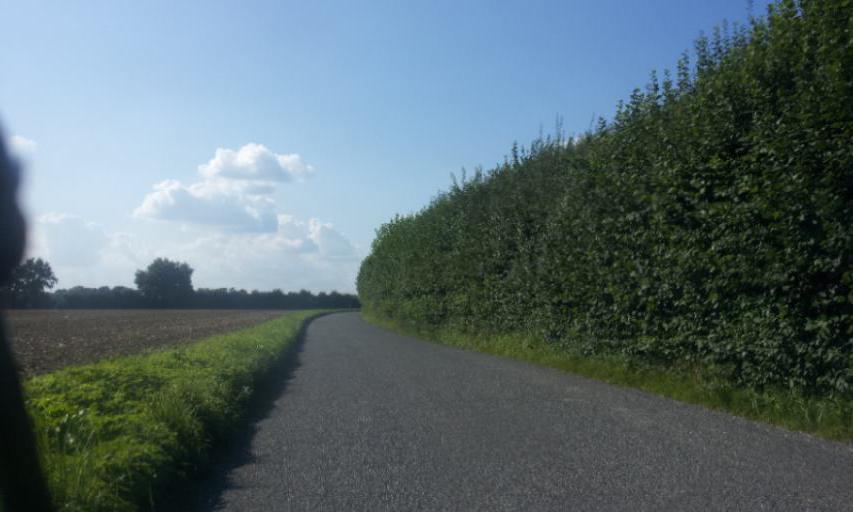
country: GB
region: England
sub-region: Kent
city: East Peckham
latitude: 51.2155
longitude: 0.3713
